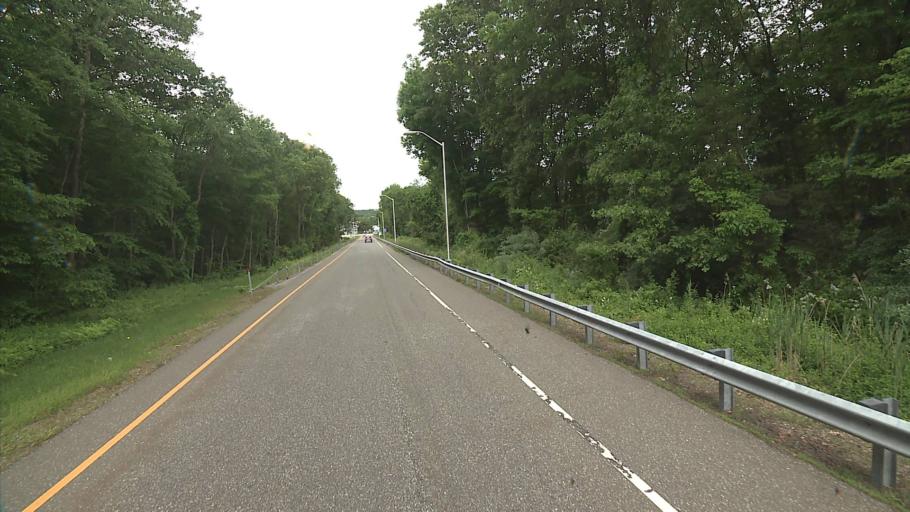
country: US
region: Connecticut
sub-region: New London County
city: Poquonock Bridge
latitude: 41.3635
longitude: -72.0235
